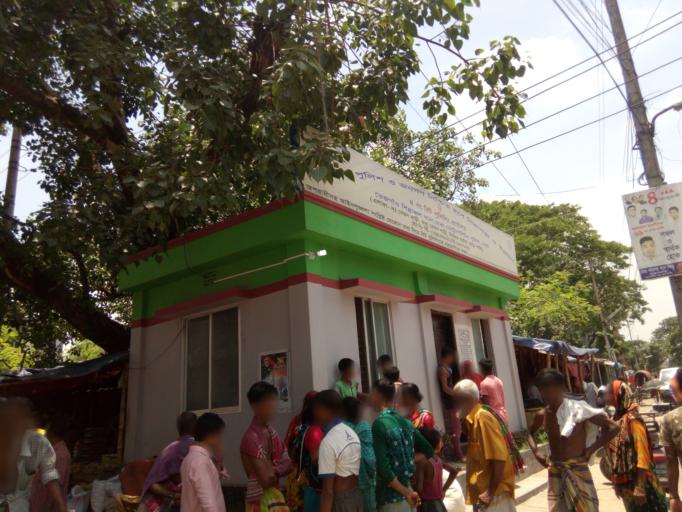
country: BD
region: Dhaka
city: Paltan
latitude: 23.7582
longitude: 90.4012
